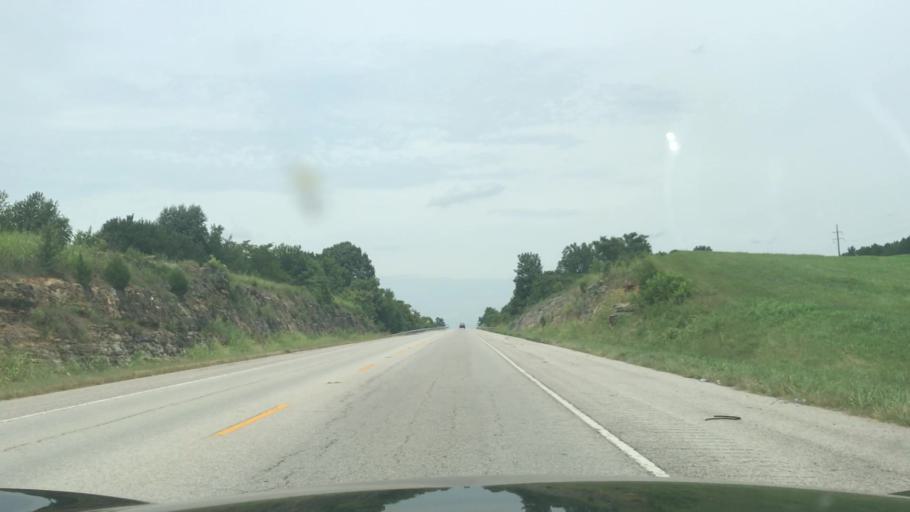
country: US
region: Kentucky
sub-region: Green County
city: Greensburg
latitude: 37.2785
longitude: -85.5126
